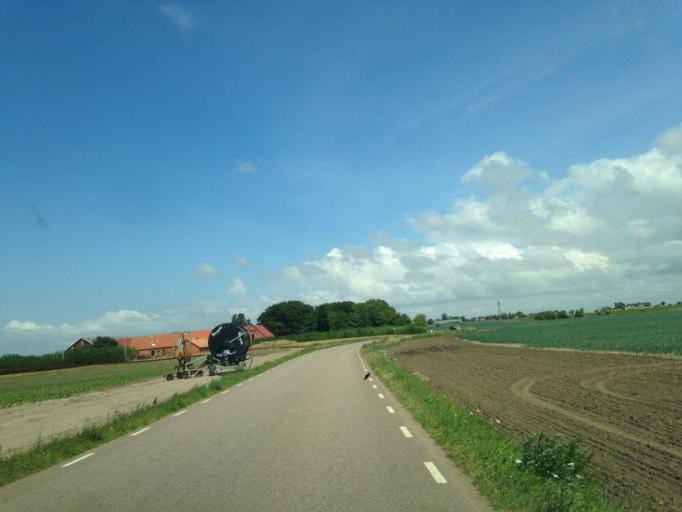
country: SE
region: Skane
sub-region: Trelleborgs Kommun
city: Skare
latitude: 55.4111
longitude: 13.0828
